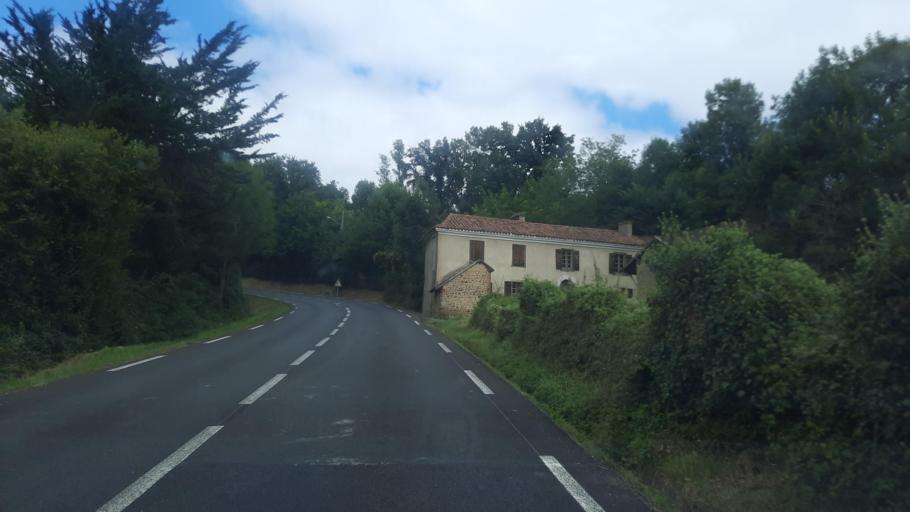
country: FR
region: Midi-Pyrenees
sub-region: Departement des Hautes-Pyrenees
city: Orleix
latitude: 43.2842
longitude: 0.1936
